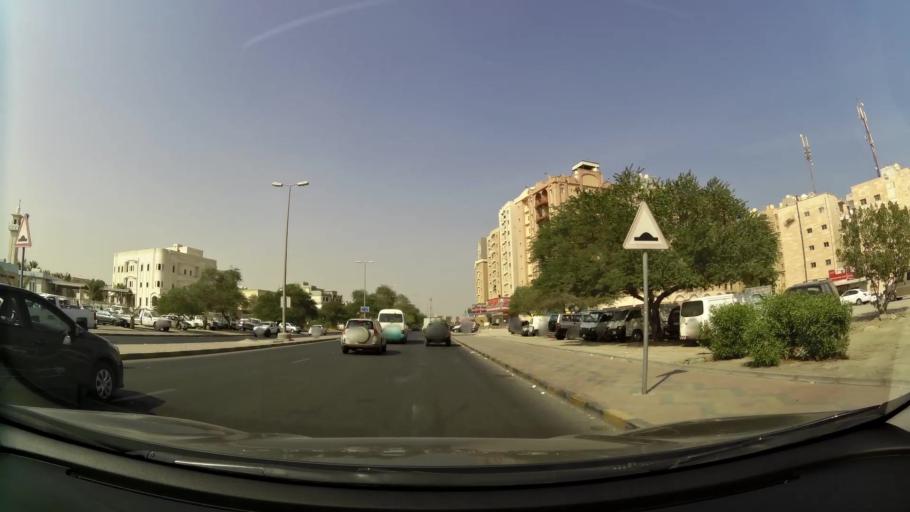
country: KW
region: Al Ahmadi
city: Al Fahahil
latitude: 29.0799
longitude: 48.1236
